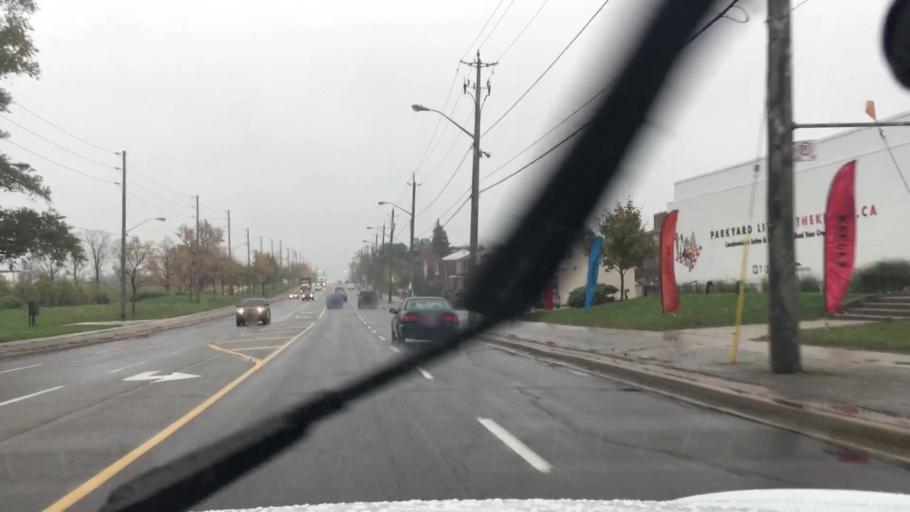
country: CA
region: Ontario
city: Concord
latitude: 43.7401
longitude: -79.4853
